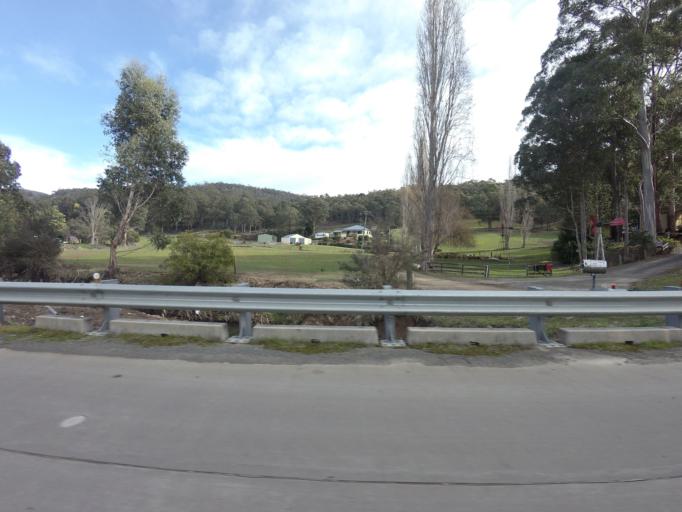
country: AU
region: Tasmania
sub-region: Kingborough
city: Margate
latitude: -42.9876
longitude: 147.1919
